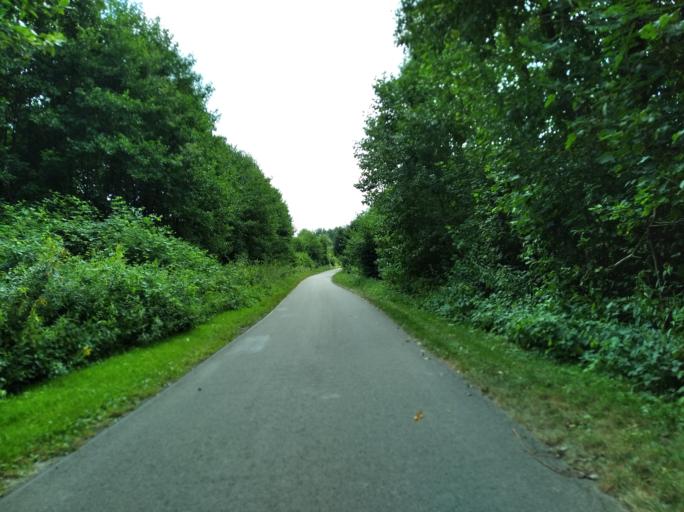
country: PL
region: Subcarpathian Voivodeship
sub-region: Powiat krosnienski
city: Leki
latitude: 49.8198
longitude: 21.6622
